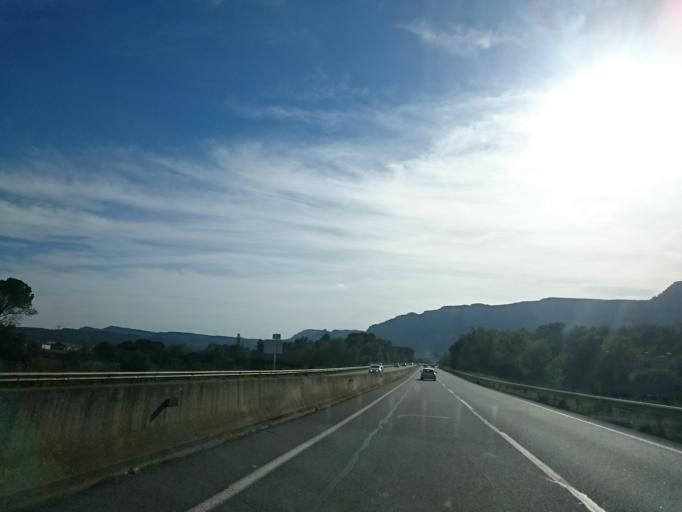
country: ES
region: Catalonia
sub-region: Provincia de Barcelona
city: Centelles
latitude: 41.8163
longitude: 2.2304
